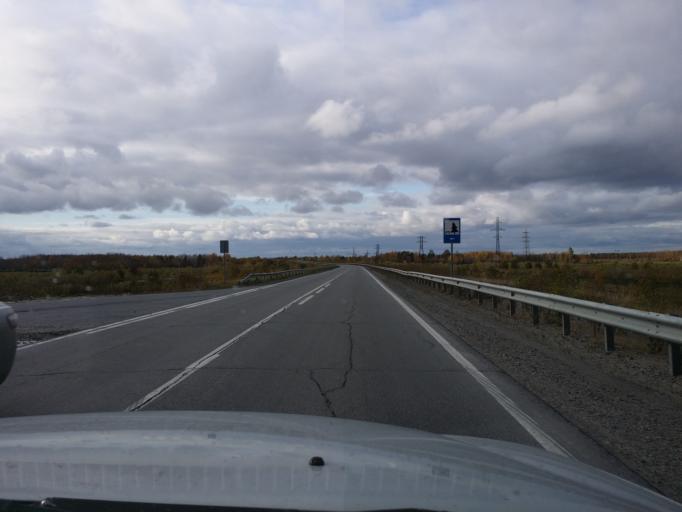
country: RU
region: Khanty-Mansiyskiy Avtonomnyy Okrug
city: Langepas
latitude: 61.1934
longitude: 75.4357
